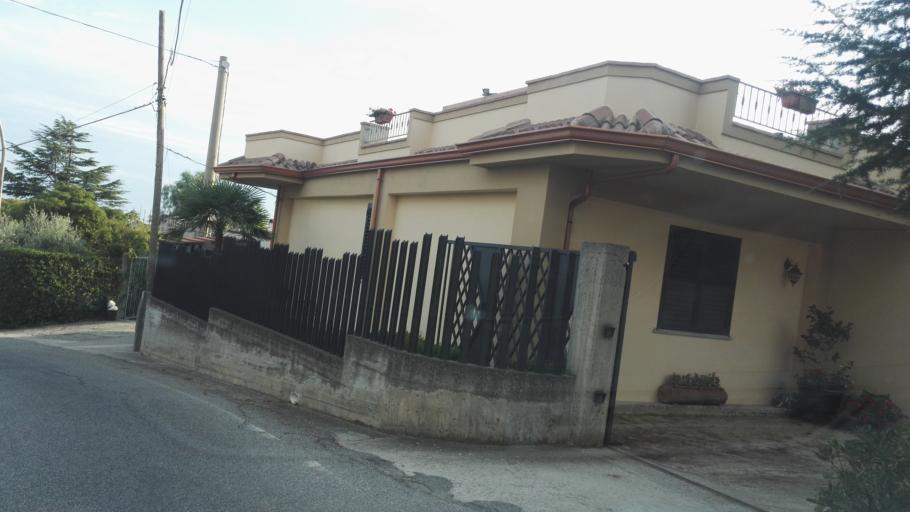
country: IT
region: Calabria
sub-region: Provincia di Reggio Calabria
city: Stignano
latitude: 38.4136
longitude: 16.4694
